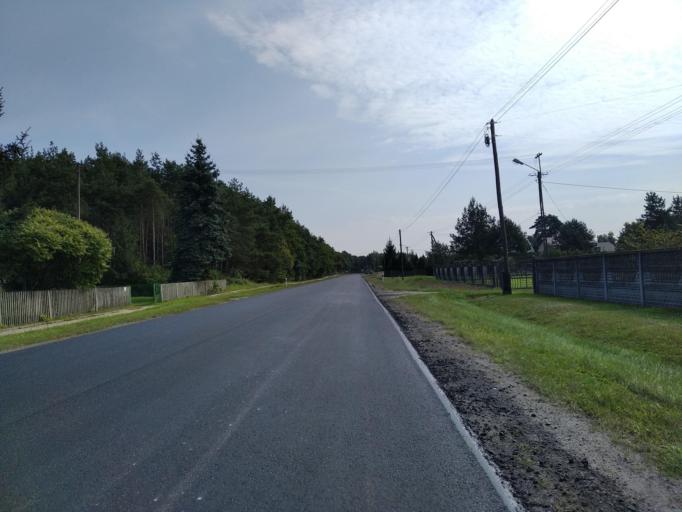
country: PL
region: Subcarpathian Voivodeship
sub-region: Powiat ropczycko-sedziszowski
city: Ostrow
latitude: 50.1578
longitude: 21.5487
